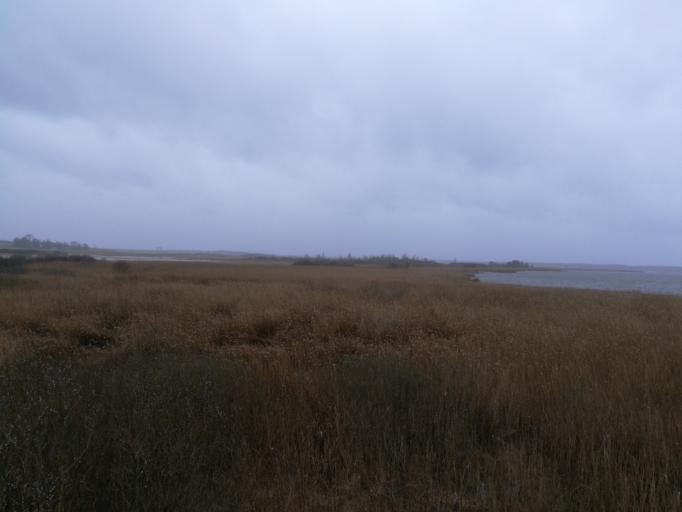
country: LT
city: Simnas
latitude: 54.4572
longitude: 23.6348
